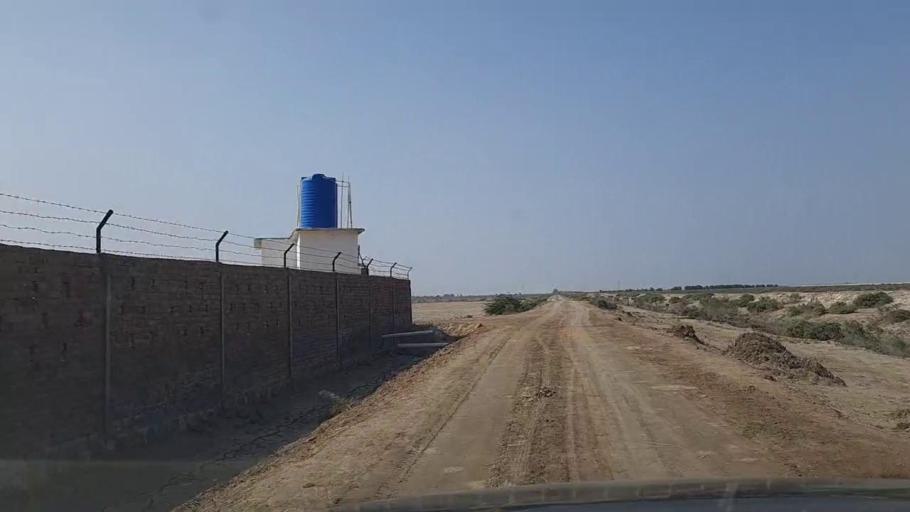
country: PK
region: Sindh
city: Gharo
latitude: 24.7046
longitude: 67.5662
